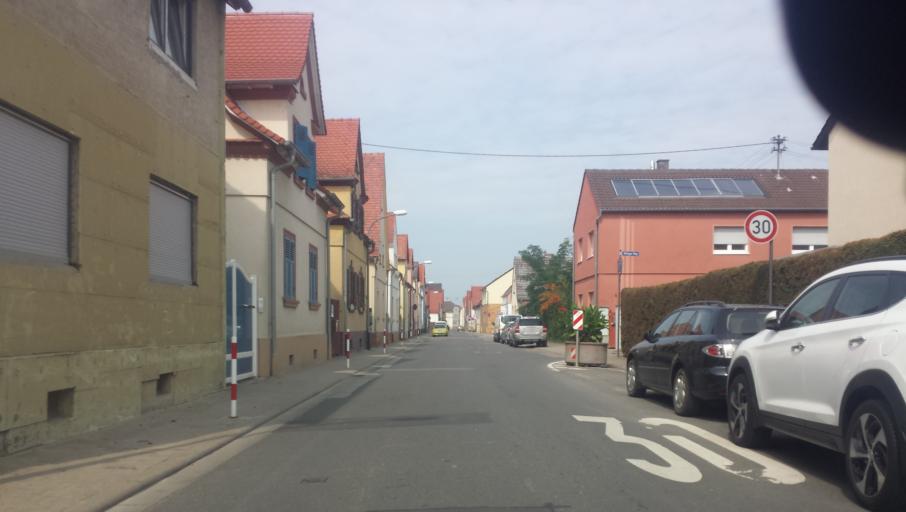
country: DE
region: Rheinland-Pfalz
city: Dannstadt-Schauernheim
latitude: 49.4684
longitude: 8.3300
